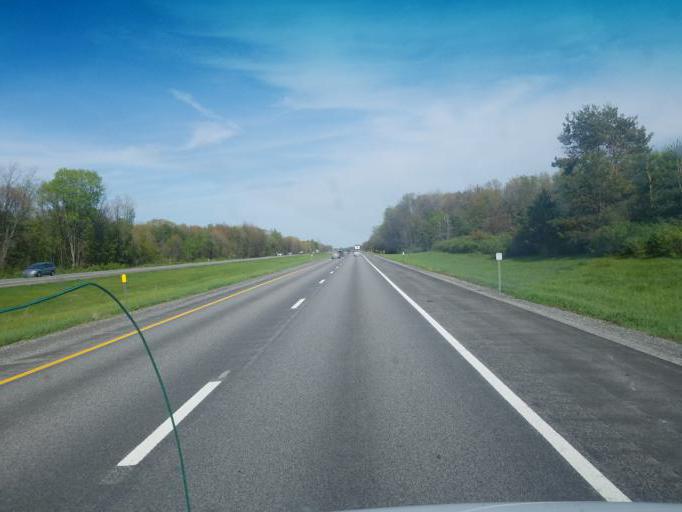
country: US
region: New York
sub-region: Madison County
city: Bolivar
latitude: 43.0916
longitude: -75.9412
